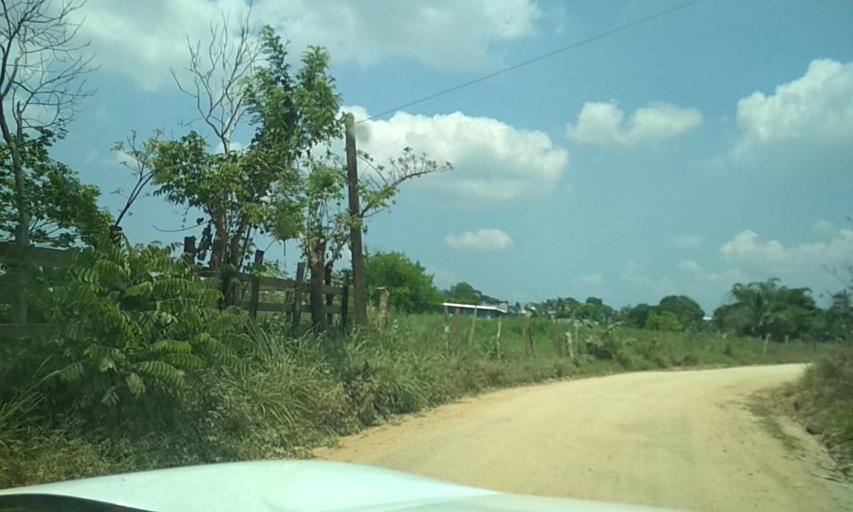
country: MX
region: Veracruz
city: Las Choapas
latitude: 17.9157
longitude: -94.0878
